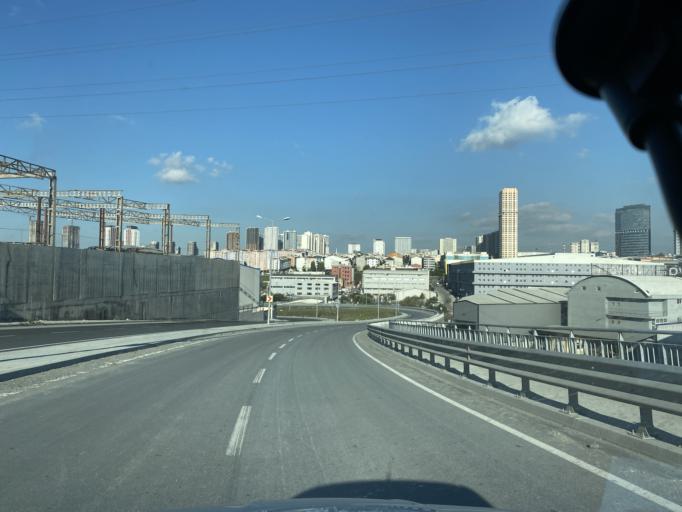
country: TR
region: Istanbul
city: Esenyurt
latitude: 41.0576
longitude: 28.6498
